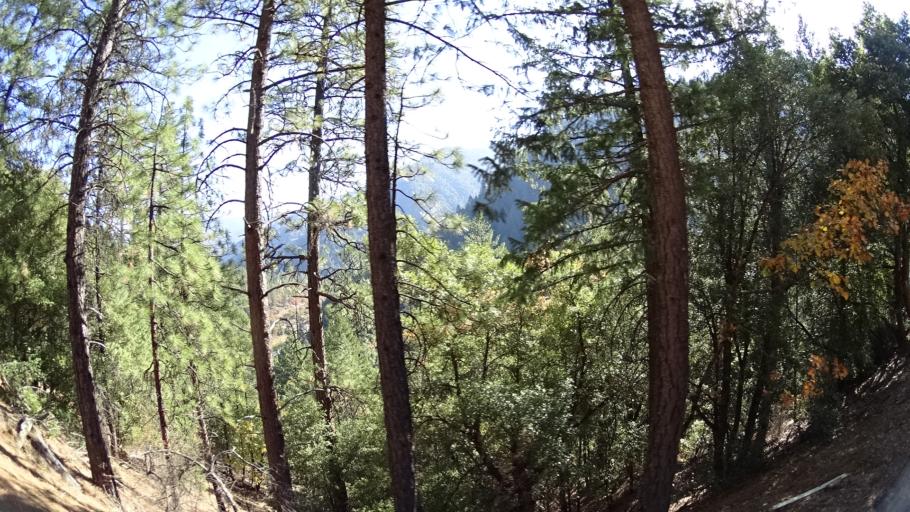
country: US
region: California
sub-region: Siskiyou County
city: Happy Camp
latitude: 41.6981
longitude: -123.0519
